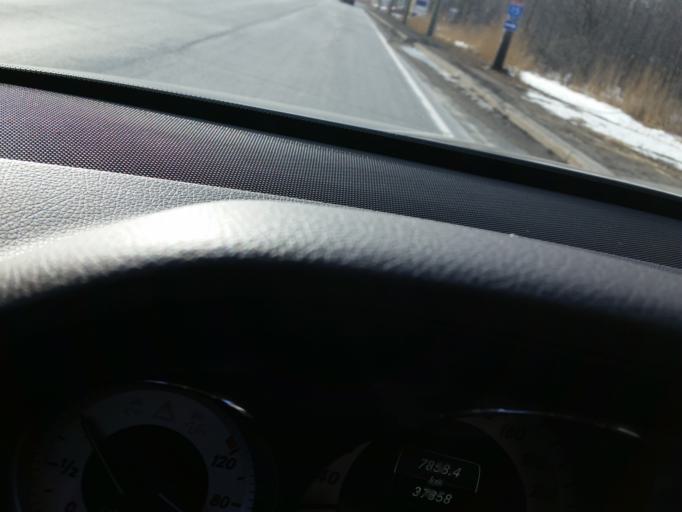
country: CA
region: Quebec
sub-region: Laurentides
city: Blainville
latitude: 45.6965
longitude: -73.9159
